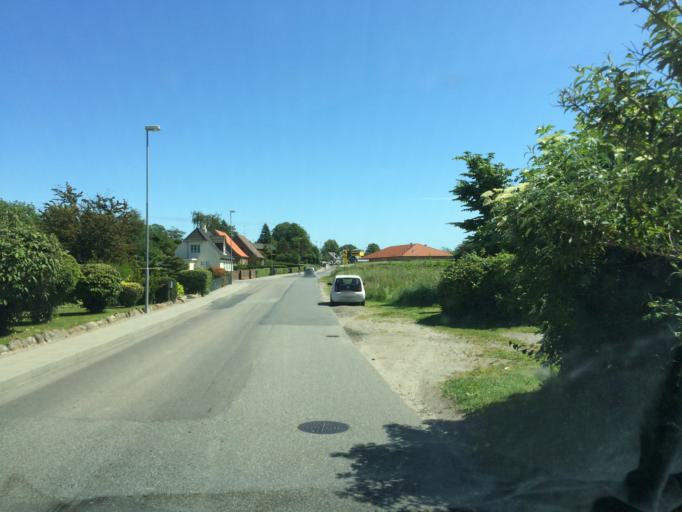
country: DK
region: Central Jutland
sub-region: Samso Kommune
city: Tranebjerg
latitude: 55.8296
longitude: 10.5916
